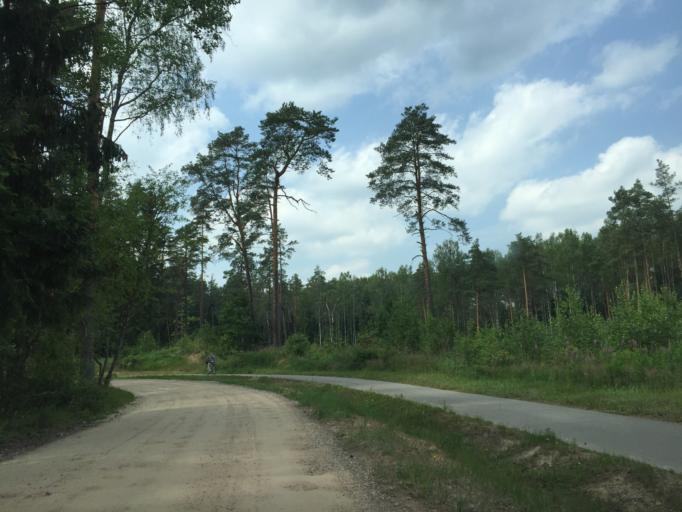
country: LV
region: Olaine
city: Olaine
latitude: 56.7795
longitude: 23.8866
